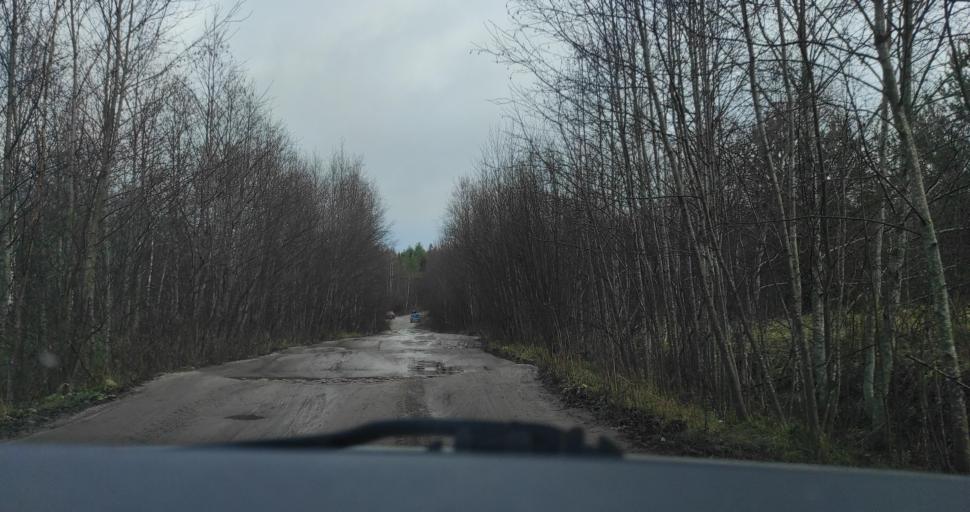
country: RU
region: Republic of Karelia
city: Pitkyaranta
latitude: 61.7347
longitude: 31.3865
